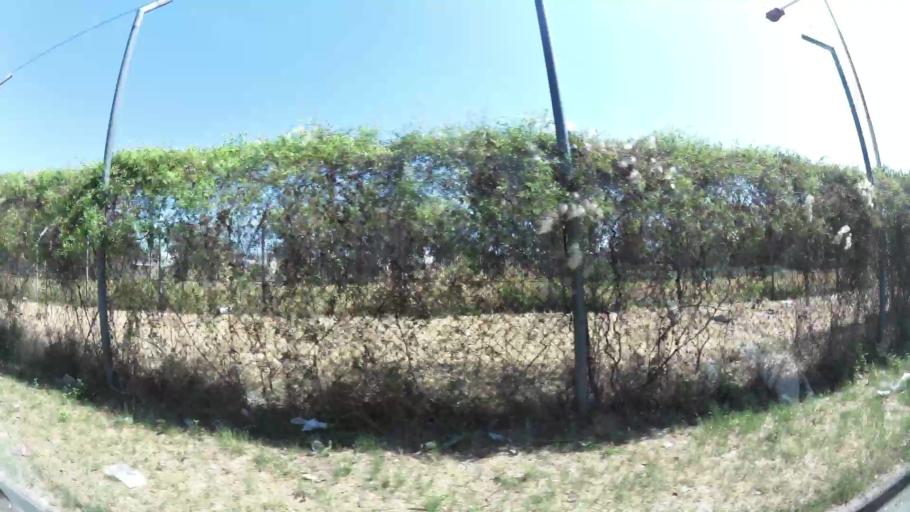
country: AR
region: Cordoba
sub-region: Departamento de Capital
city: Cordoba
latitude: -31.4559
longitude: -64.1628
